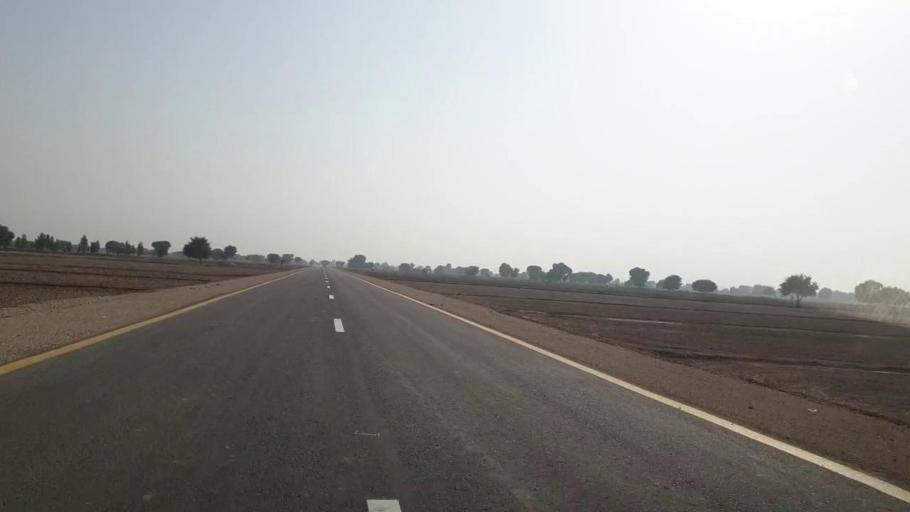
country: PK
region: Sindh
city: Bhan
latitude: 26.5158
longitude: 67.7863
